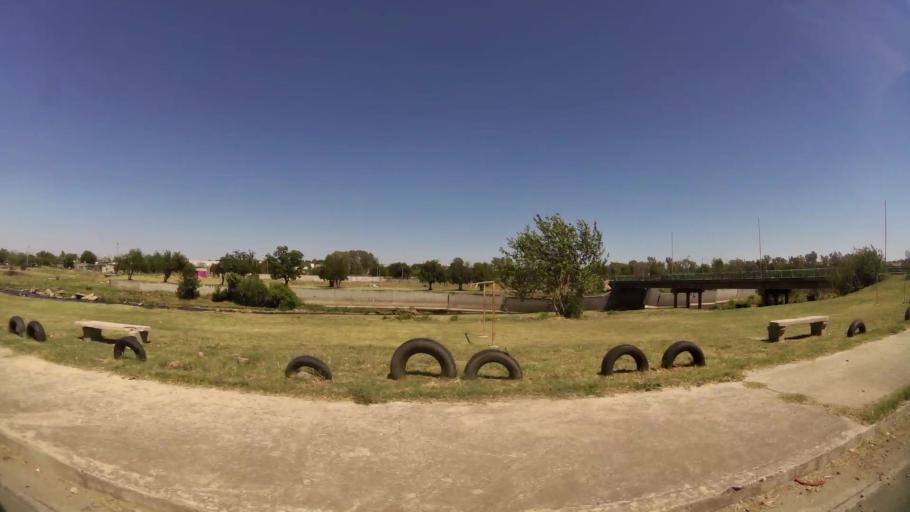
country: AR
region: Cordoba
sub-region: Departamento de Capital
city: Cordoba
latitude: -31.4115
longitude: -64.1408
